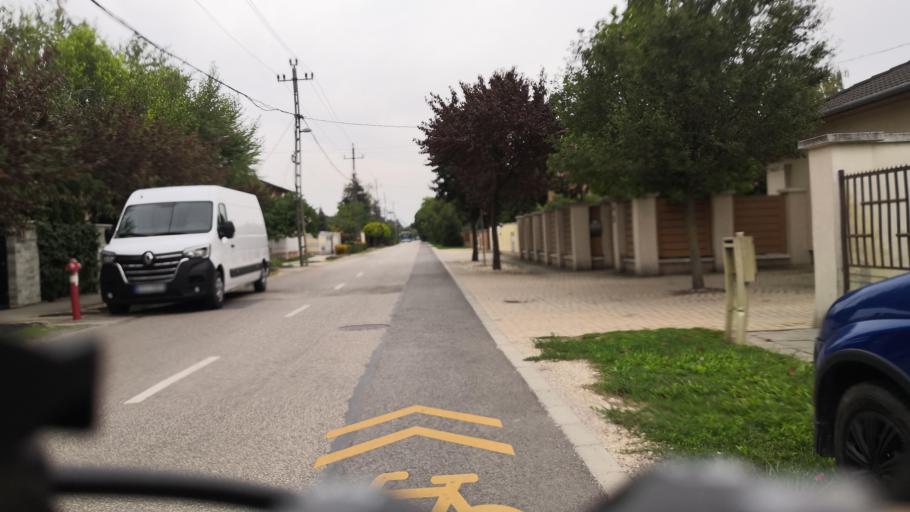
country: HU
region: Csongrad
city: Szeged
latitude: 46.2861
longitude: 20.1647
